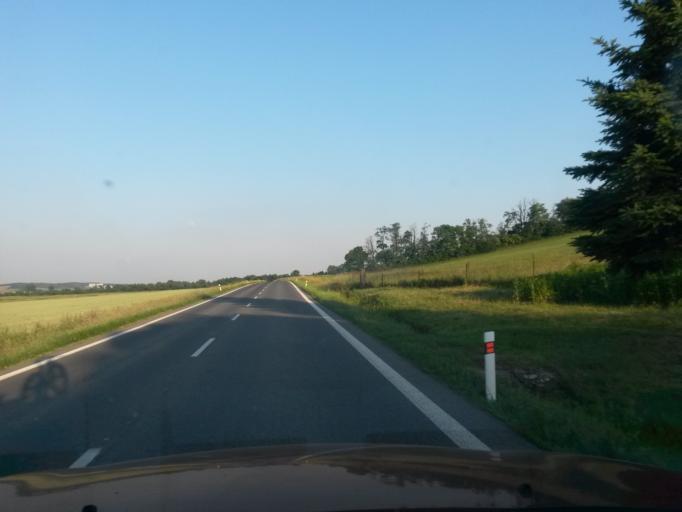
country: SK
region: Presovsky
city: Vranov nad Topl'ou
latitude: 48.9180
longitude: 21.6082
